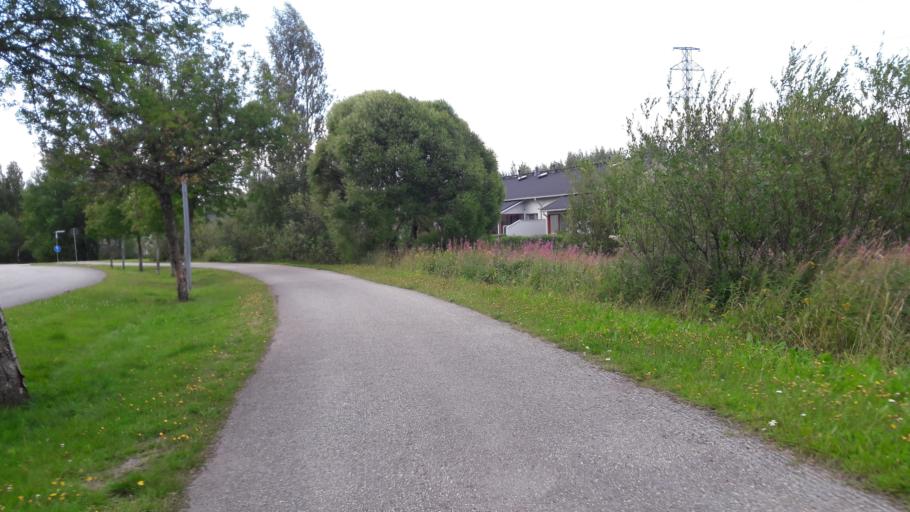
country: FI
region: North Karelia
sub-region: Joensuu
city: Joensuu
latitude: 62.5909
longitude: 29.8053
